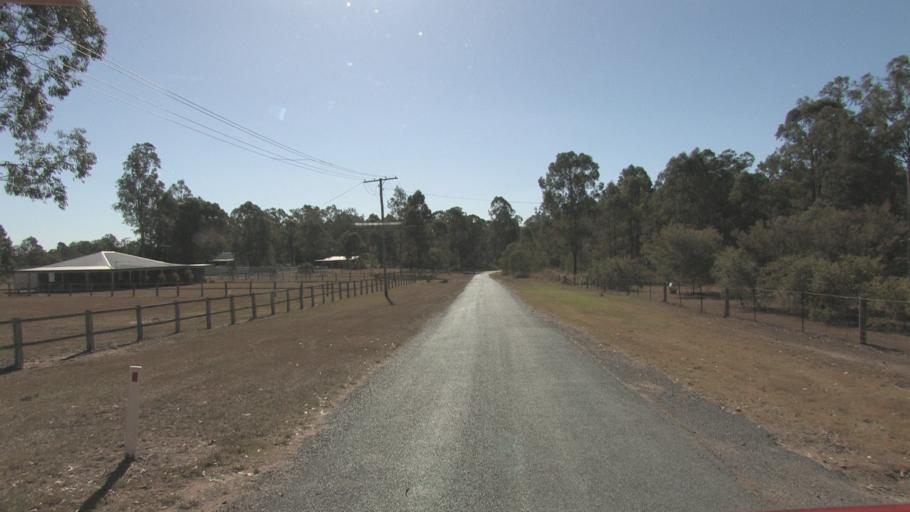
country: AU
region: Queensland
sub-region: Logan
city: Cedar Vale
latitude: -27.8659
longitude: 153.0266
